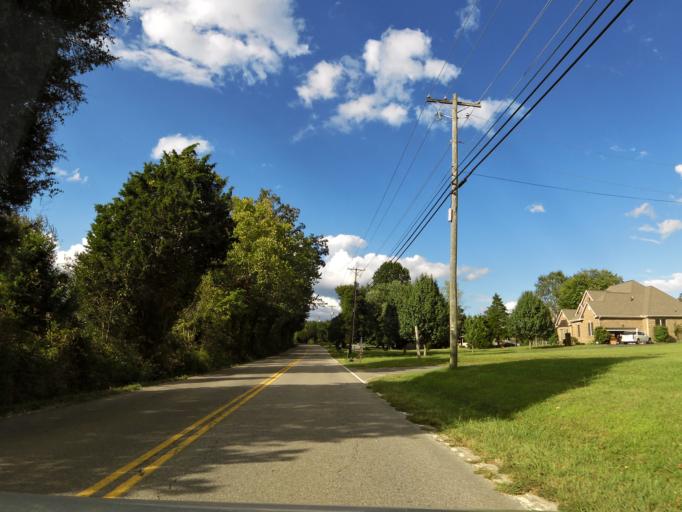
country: US
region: Tennessee
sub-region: Knox County
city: Mascot
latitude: 36.0980
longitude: -83.8162
